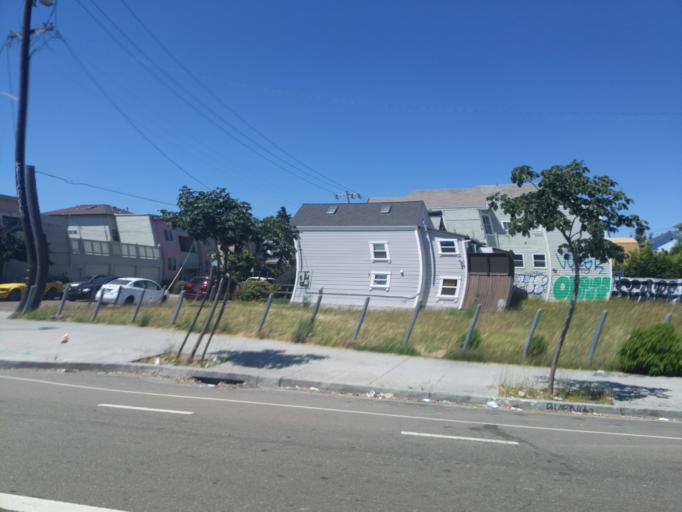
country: US
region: California
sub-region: Alameda County
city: Oakland
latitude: 37.8057
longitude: -122.2968
